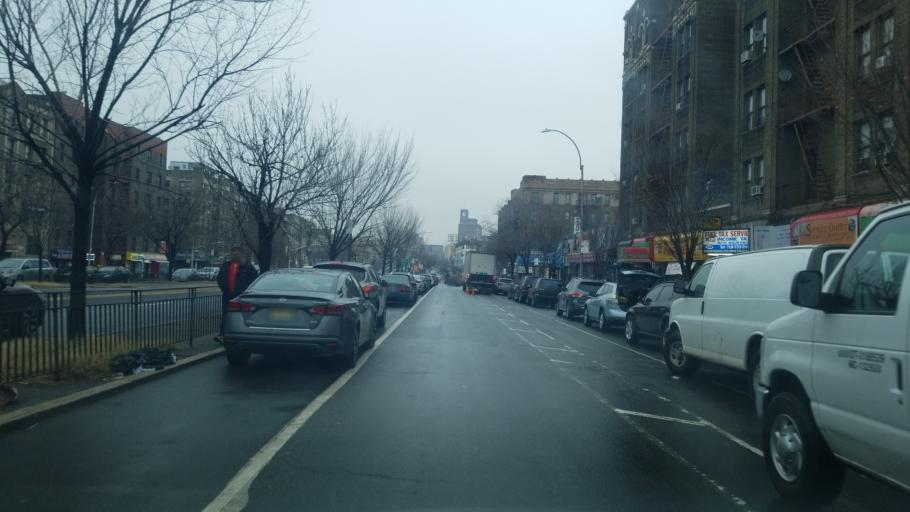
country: US
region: New York
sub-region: New York County
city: Inwood
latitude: 40.8577
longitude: -73.8997
